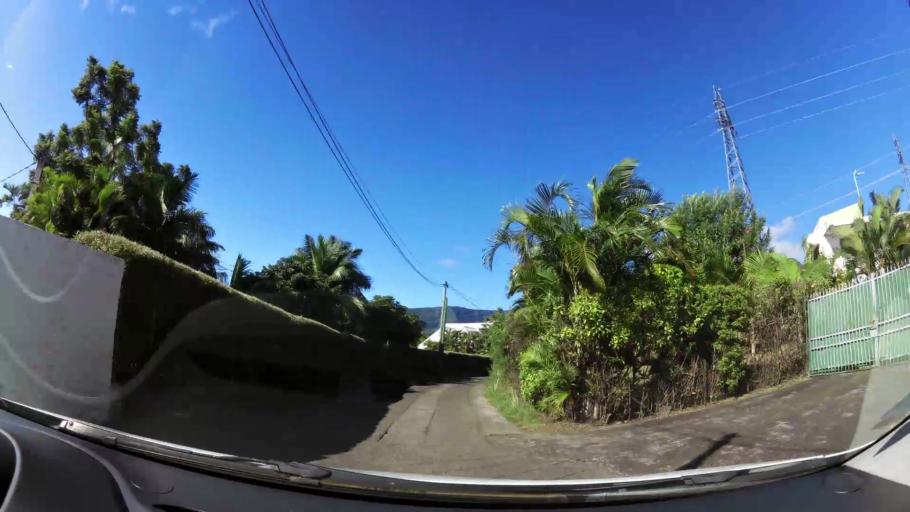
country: RE
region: Reunion
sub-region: Reunion
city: Saint-Denis
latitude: -20.9184
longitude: 55.4789
